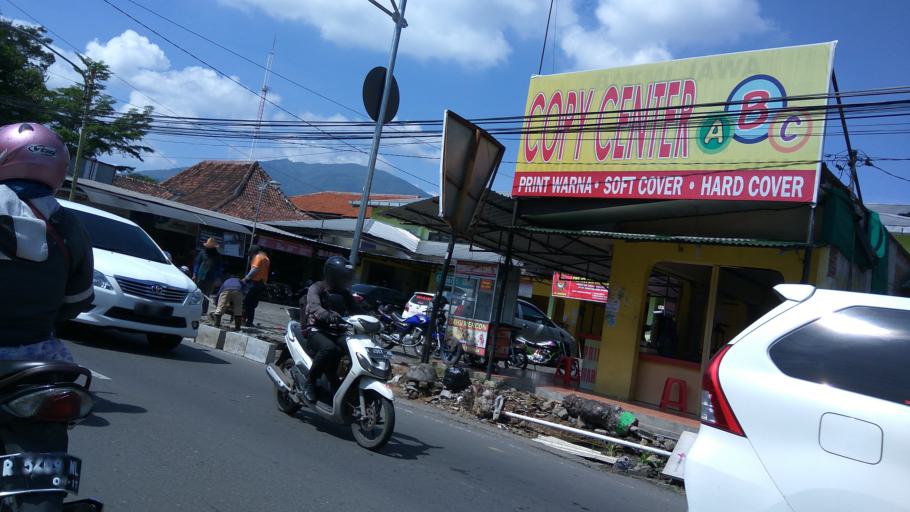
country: ID
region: Central Java
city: Ungaran
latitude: -7.1290
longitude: 110.4091
